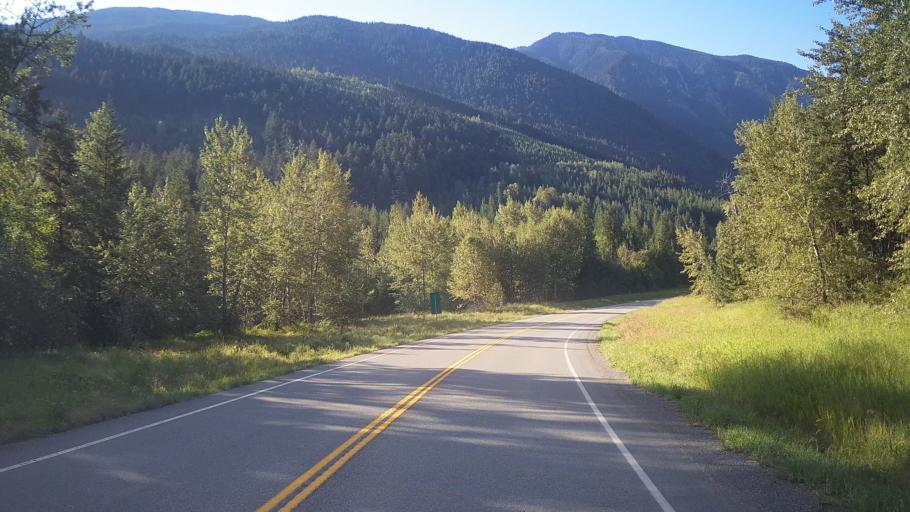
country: CA
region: British Columbia
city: Lillooet
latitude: 50.5810
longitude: -122.0882
